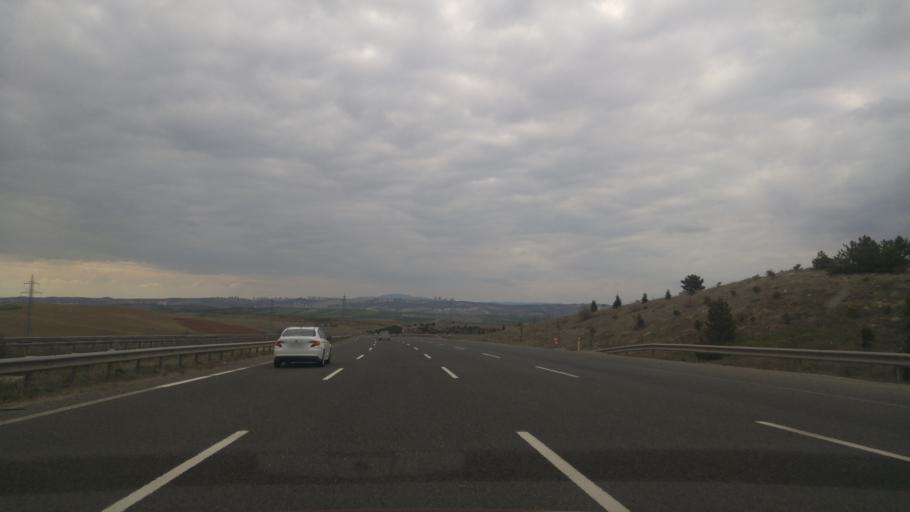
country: TR
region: Ankara
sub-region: Goelbasi
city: Golbasi
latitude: 39.7962
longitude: 32.6546
